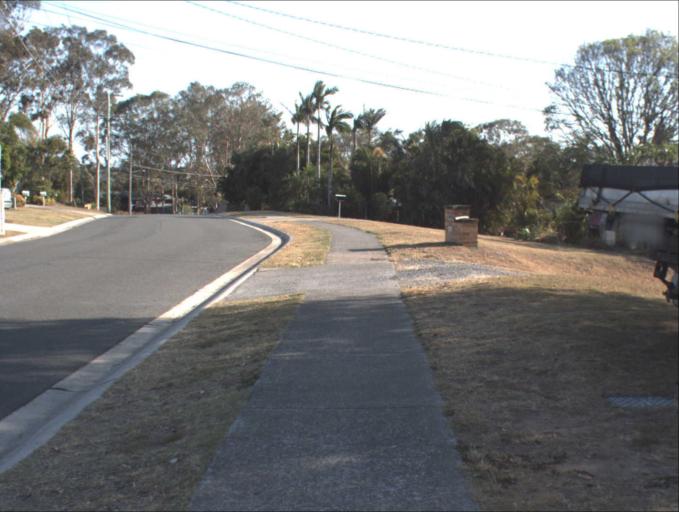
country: AU
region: Queensland
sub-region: Logan
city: Beenleigh
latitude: -27.6921
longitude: 153.1756
